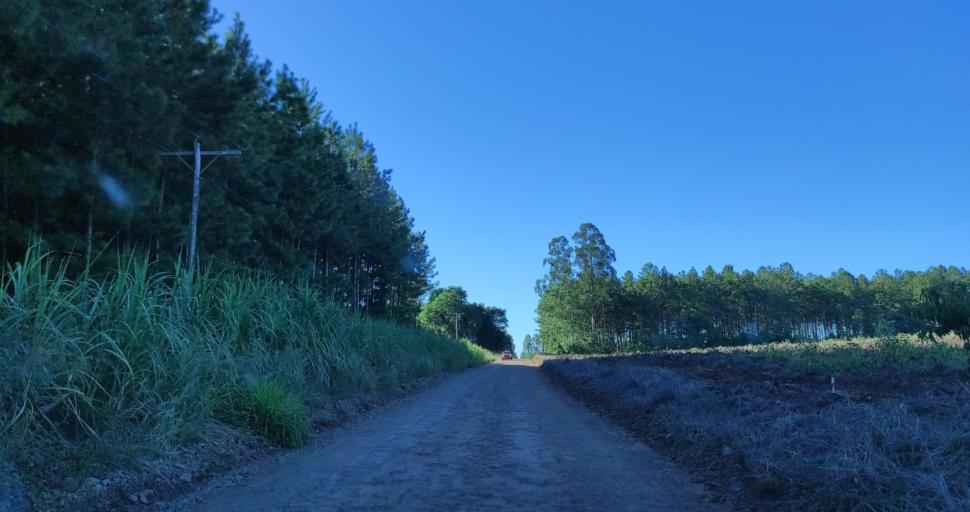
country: AR
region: Misiones
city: Capiovi
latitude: -26.8863
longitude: -54.9969
